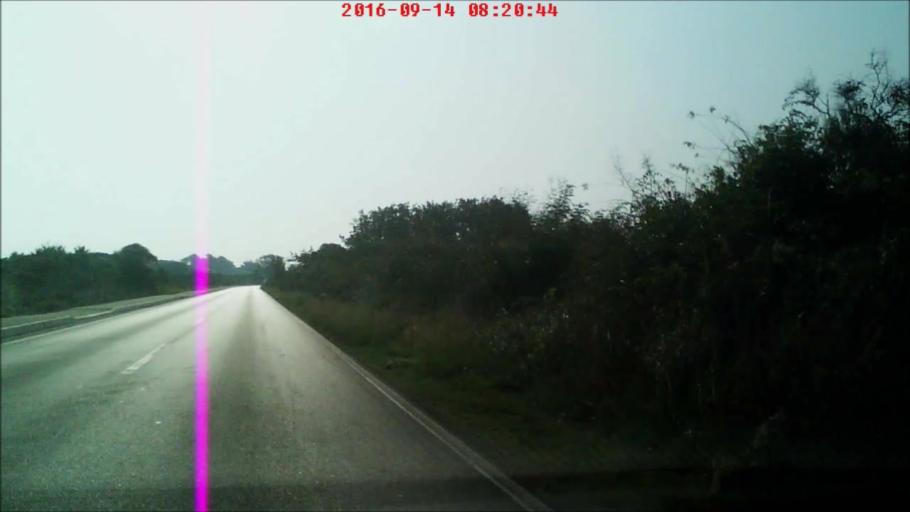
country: HR
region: Zadarska
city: Nin
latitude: 44.2253
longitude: 15.2037
